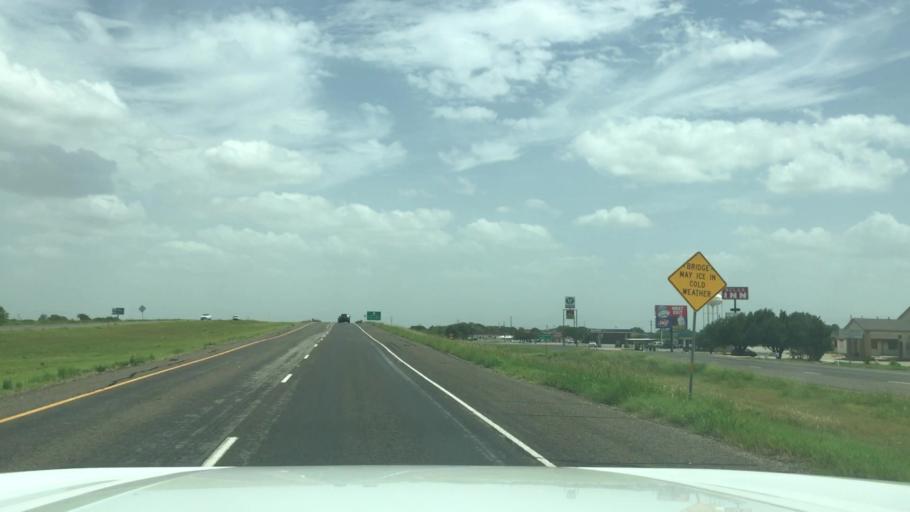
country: US
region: Texas
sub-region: Falls County
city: Marlin
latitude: 31.3227
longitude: -96.8850
